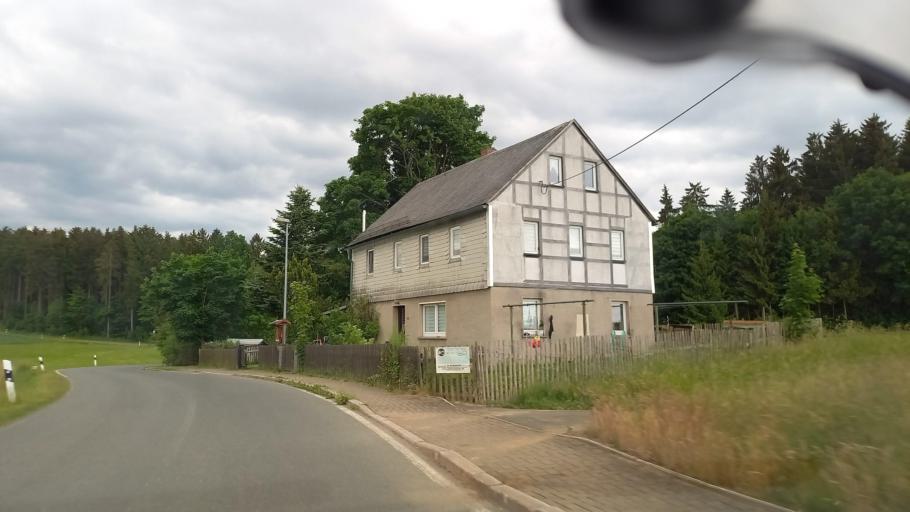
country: DE
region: Saxony
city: Waldkirchen
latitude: 50.6252
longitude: 12.3976
